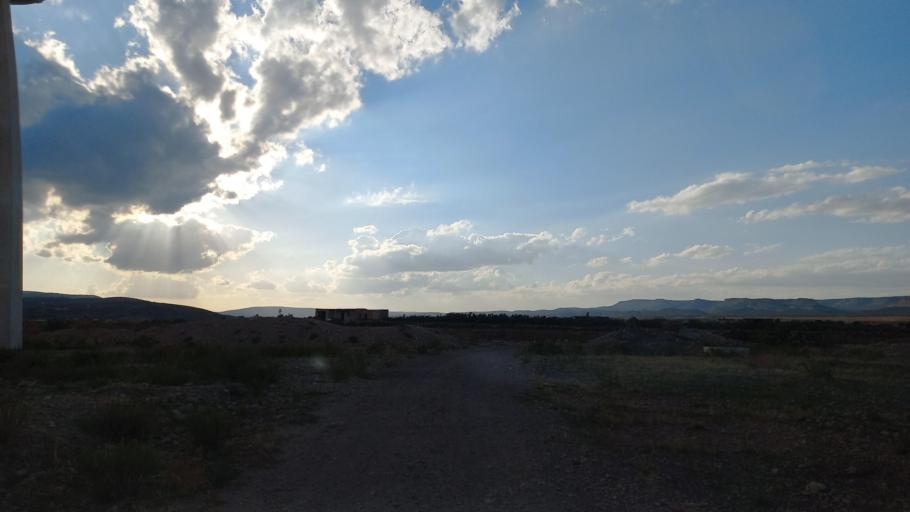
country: TN
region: Al Qasrayn
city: Sbiba
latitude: 35.3904
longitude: 9.0458
